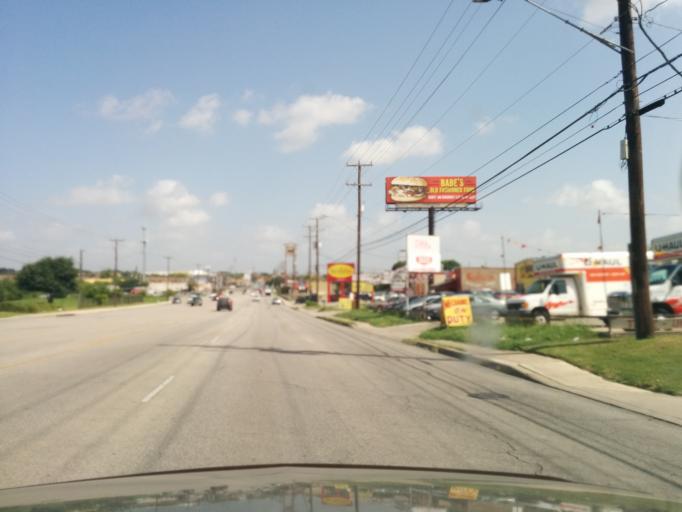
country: US
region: Texas
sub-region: Bexar County
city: Leon Valley
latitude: 29.5201
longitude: -98.5971
